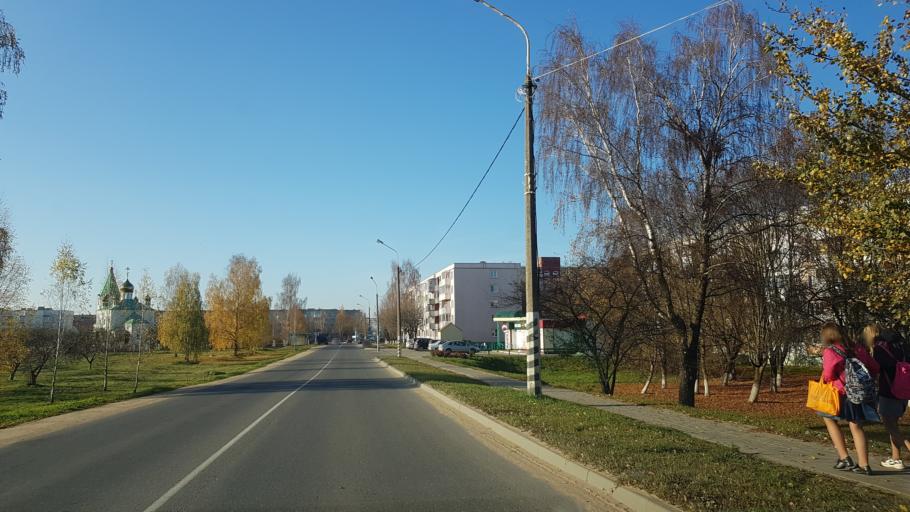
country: BY
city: Fanipol
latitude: 53.7379
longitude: 27.3199
